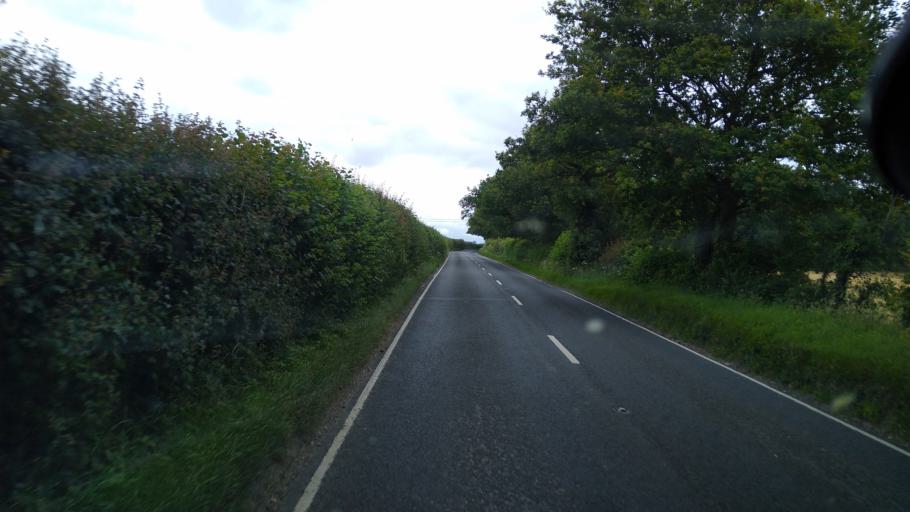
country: GB
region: England
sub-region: Hampshire
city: Alton
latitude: 51.1293
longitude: -0.9594
